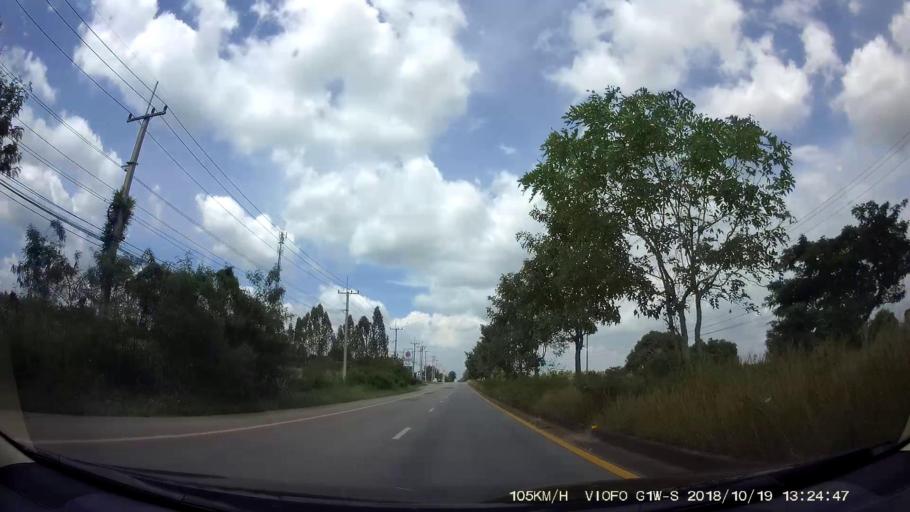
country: TH
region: Chaiyaphum
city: Chatturat
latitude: 15.5120
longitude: 101.8232
